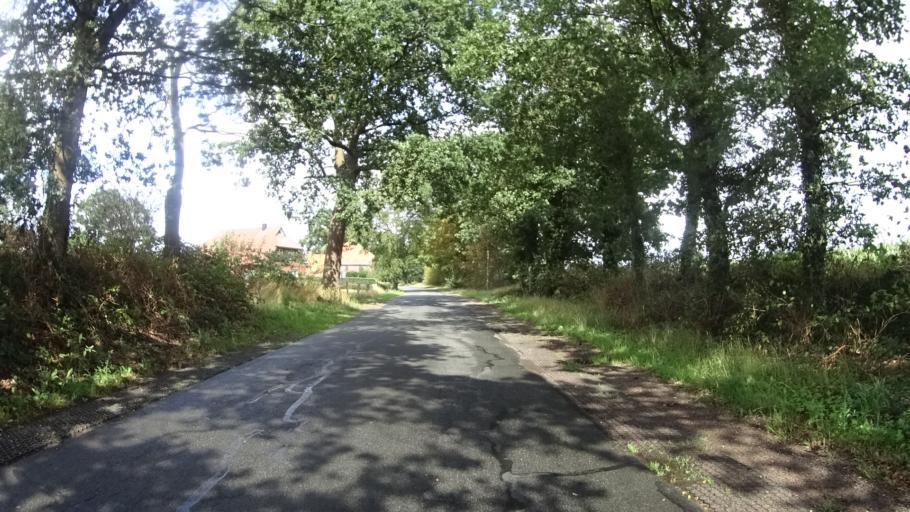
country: DE
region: Lower Saxony
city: Zetel
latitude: 53.3906
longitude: 7.9232
